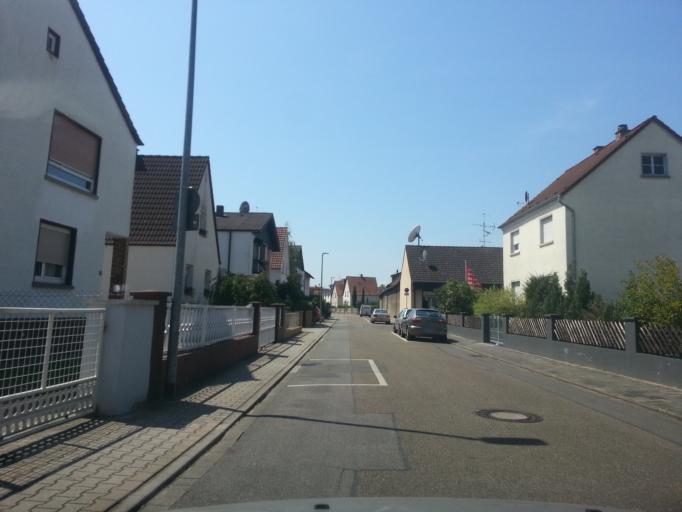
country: DE
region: Hesse
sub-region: Regierungsbezirk Darmstadt
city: Biblis
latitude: 49.6880
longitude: 8.4597
